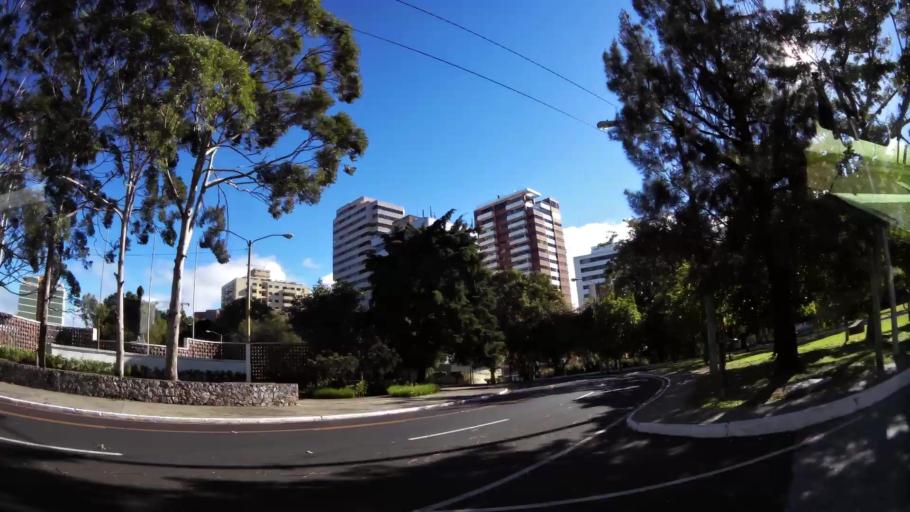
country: GT
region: Guatemala
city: Santa Catarina Pinula
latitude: 14.5726
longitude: -90.5255
